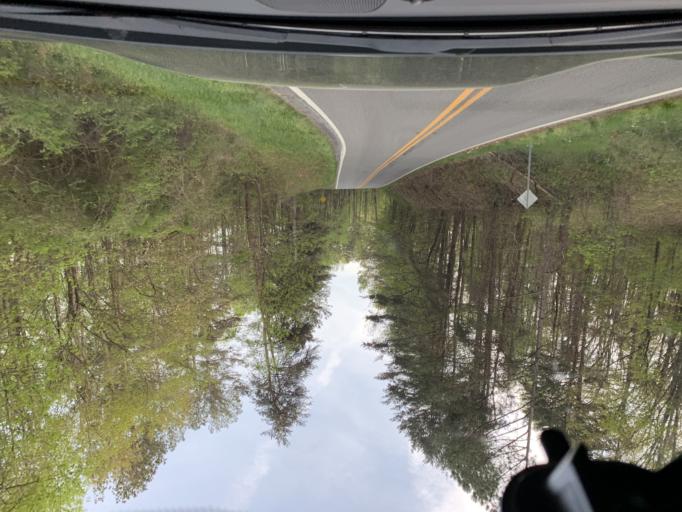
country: US
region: Georgia
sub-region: Forsyth County
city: Cumming
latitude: 34.2496
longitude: -84.1453
